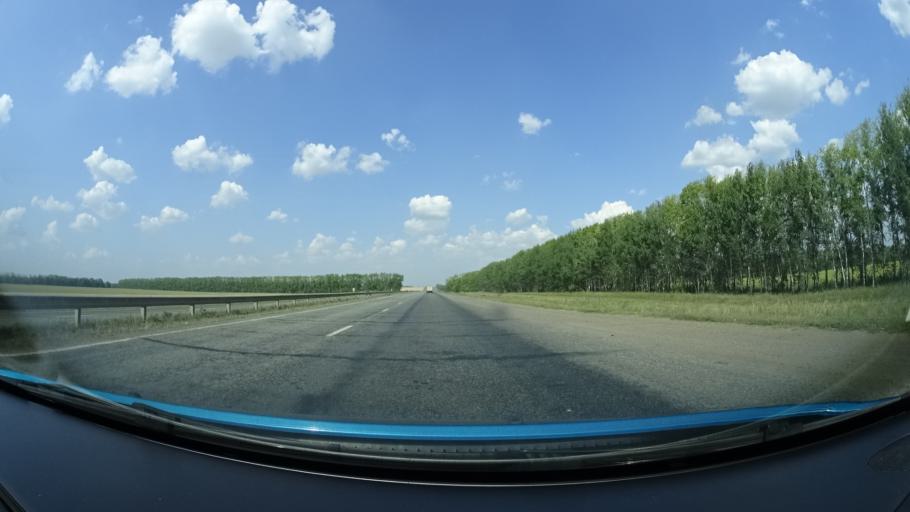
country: RU
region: Bashkortostan
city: Dmitriyevka
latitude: 54.6941
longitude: 55.2822
